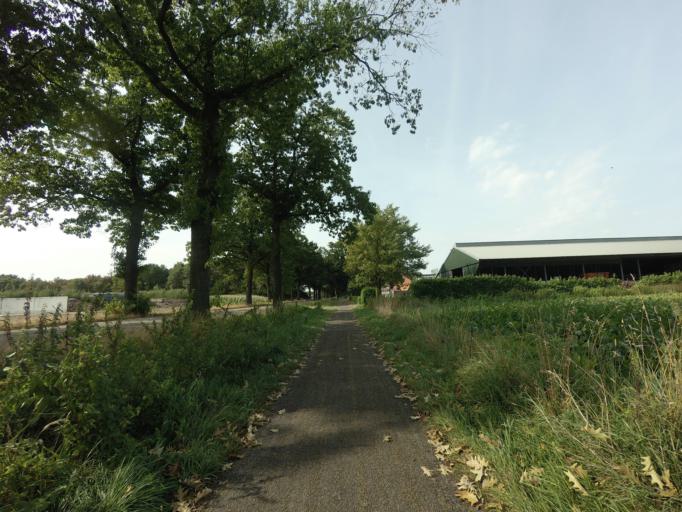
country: NL
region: North Brabant
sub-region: Gemeente Sint Anthonis
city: Sint Anthonis
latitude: 51.5834
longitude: 5.8428
